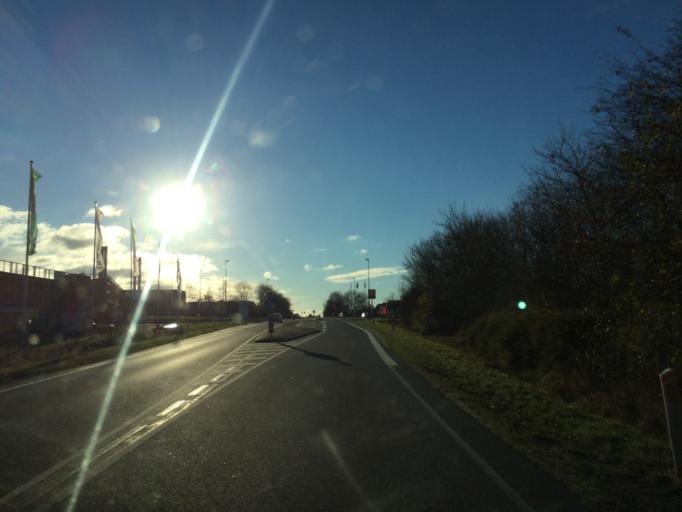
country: DK
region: Central Jutland
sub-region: Herning Kommune
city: Kibaek
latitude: 56.0326
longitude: 8.8614
